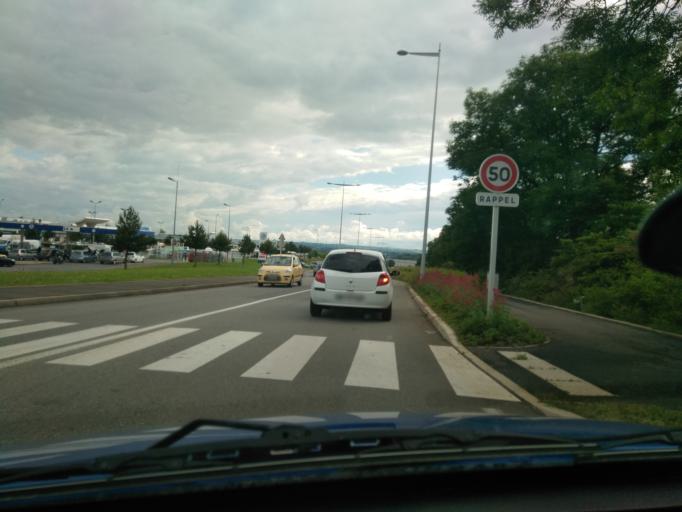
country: FR
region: Midi-Pyrenees
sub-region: Departement de l'Aveyron
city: Sebazac-Concoures
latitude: 44.3950
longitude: 2.6032
